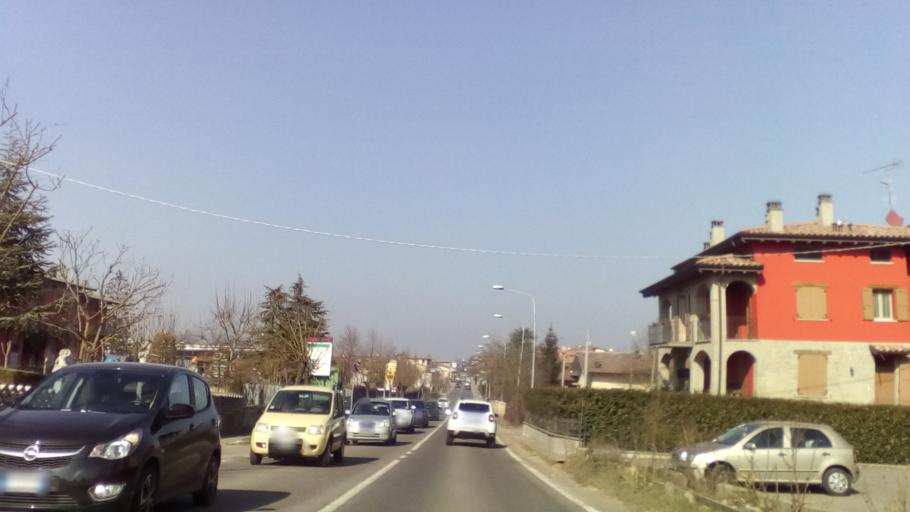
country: IT
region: Emilia-Romagna
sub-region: Provincia di Modena
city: Sant'Antonio
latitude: 44.3656
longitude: 10.8347
